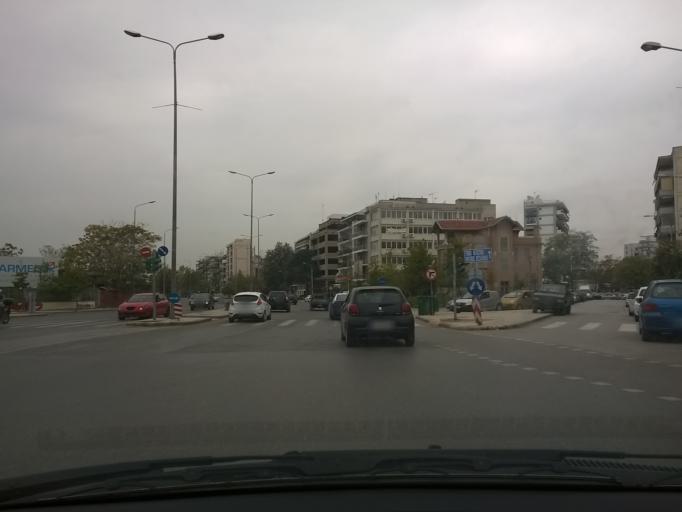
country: GR
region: Central Macedonia
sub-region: Nomos Thessalonikis
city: Thessaloniki
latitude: 40.6396
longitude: 22.9310
